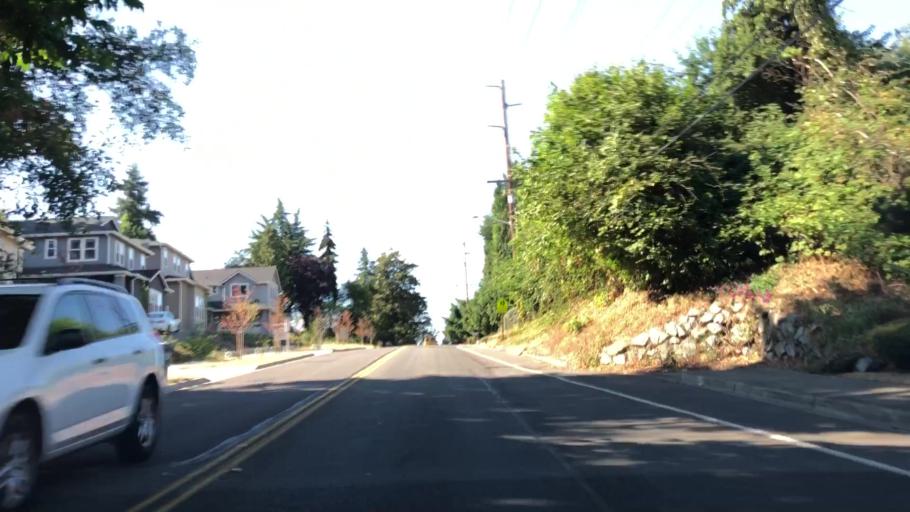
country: US
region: Washington
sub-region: King County
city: East Hill-Meridian
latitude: 47.4256
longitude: -122.2138
